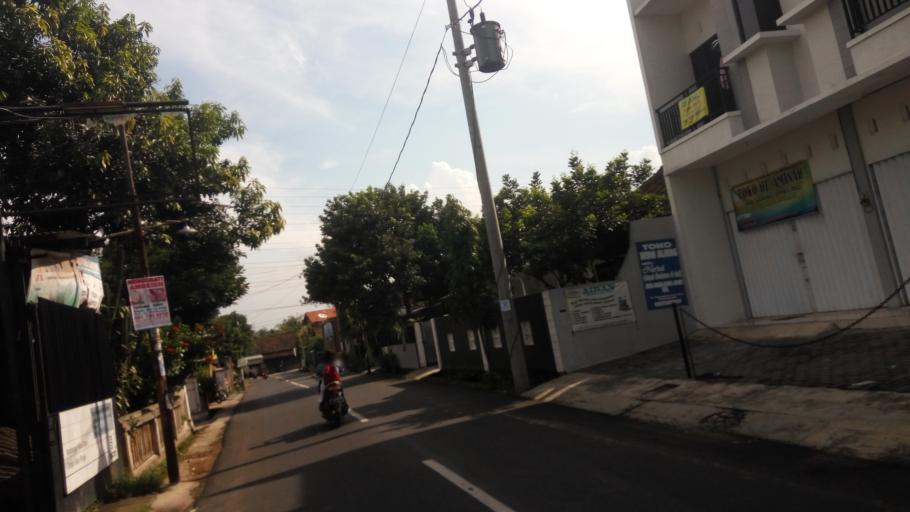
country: ID
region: Central Java
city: Ungaran
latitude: -7.1494
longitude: 110.4218
